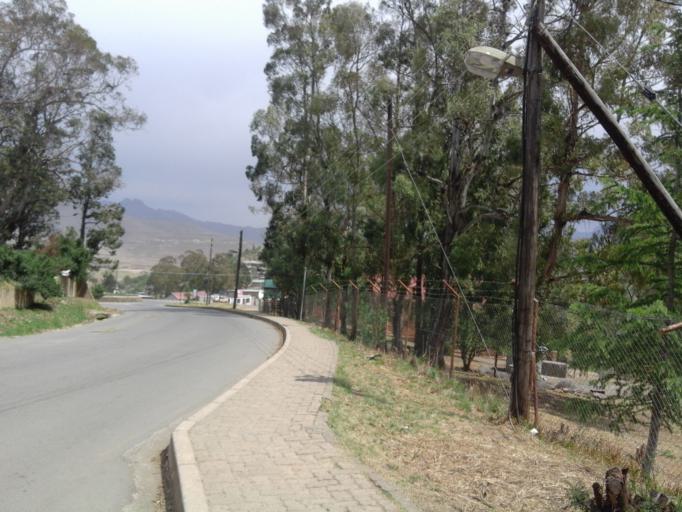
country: LS
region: Qacha's Nek
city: Qacha's Nek
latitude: -30.1198
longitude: 28.6875
